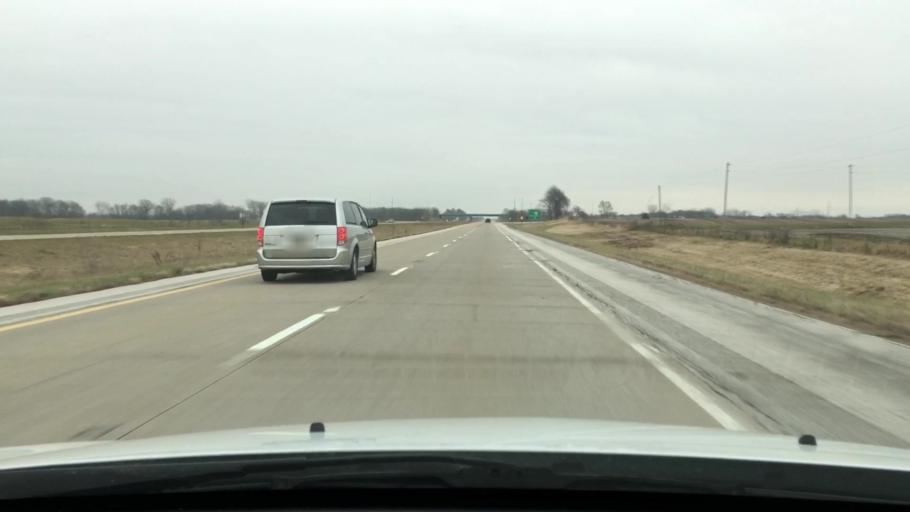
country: US
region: Illinois
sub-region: Scott County
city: Winchester
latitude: 39.6809
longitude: -90.4675
